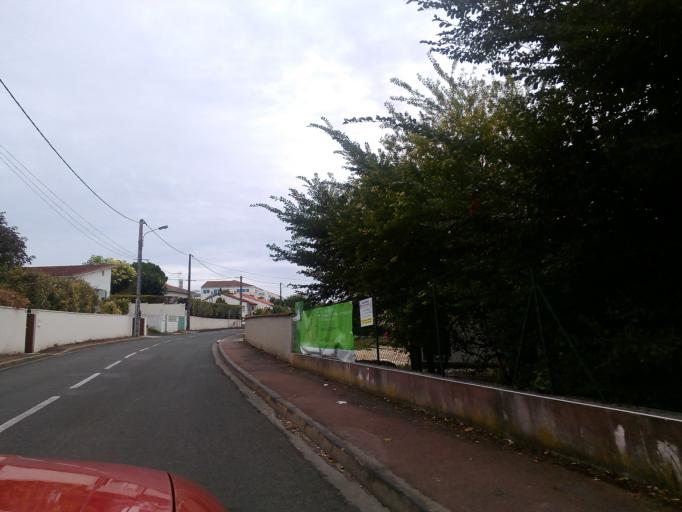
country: FR
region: Poitou-Charentes
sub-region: Departement de la Charente-Maritime
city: Vaux-sur-Mer
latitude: 45.6444
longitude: -1.0613
